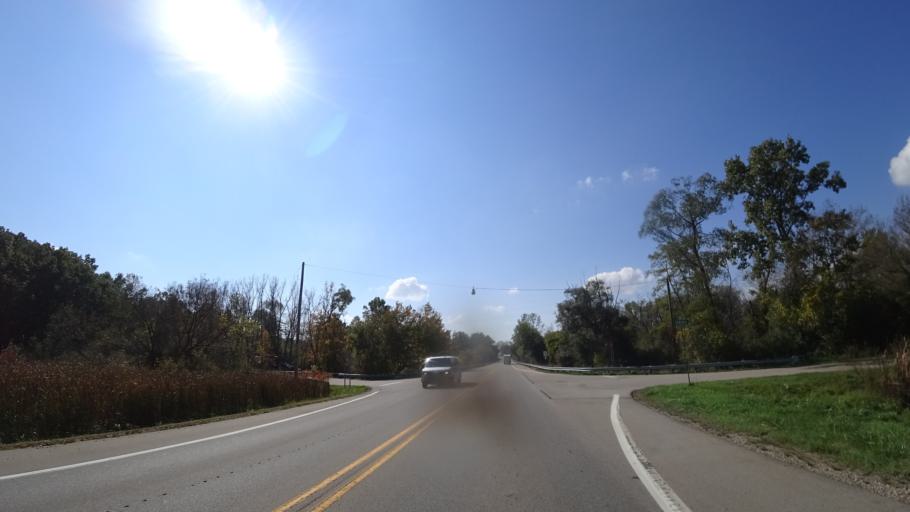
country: US
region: Michigan
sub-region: Jackson County
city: Concord
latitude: 42.1802
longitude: -84.6484
